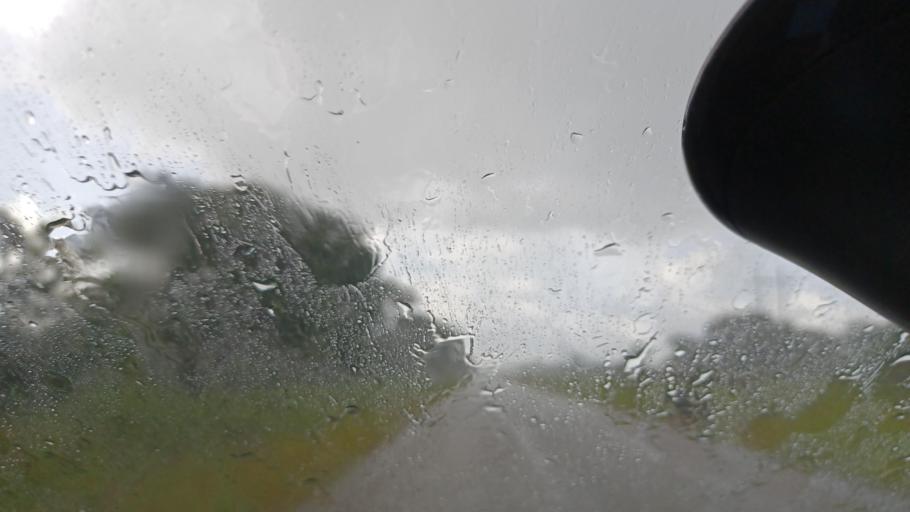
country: ZM
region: North-Western
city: Kasempa
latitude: -13.0962
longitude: 25.9107
